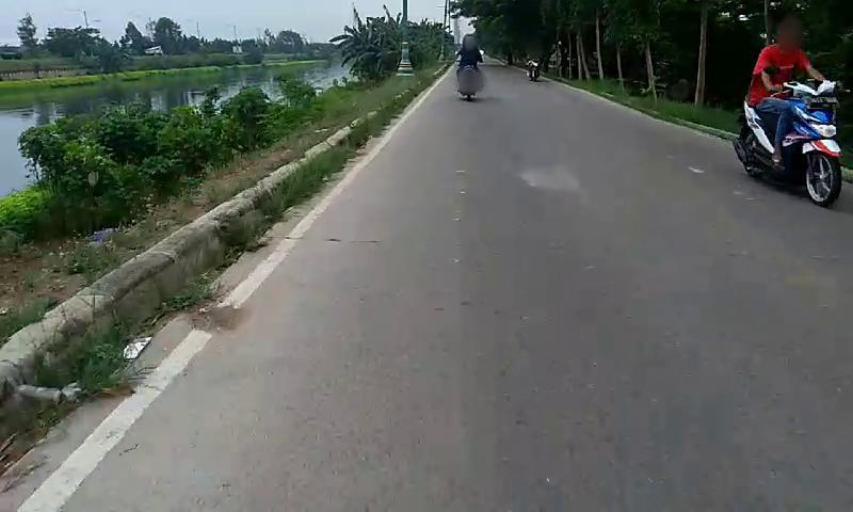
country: ID
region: West Java
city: Bekasi
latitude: -6.1400
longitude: 106.9695
